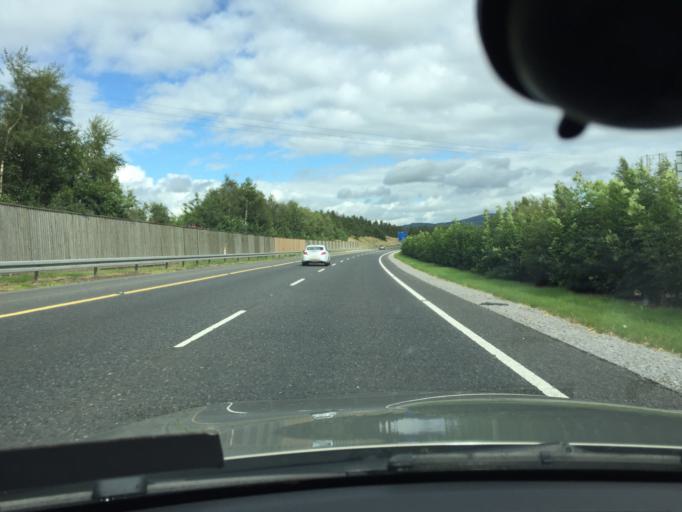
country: IE
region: Leinster
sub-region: Lu
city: Dundalk
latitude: 54.0309
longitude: -6.4312
